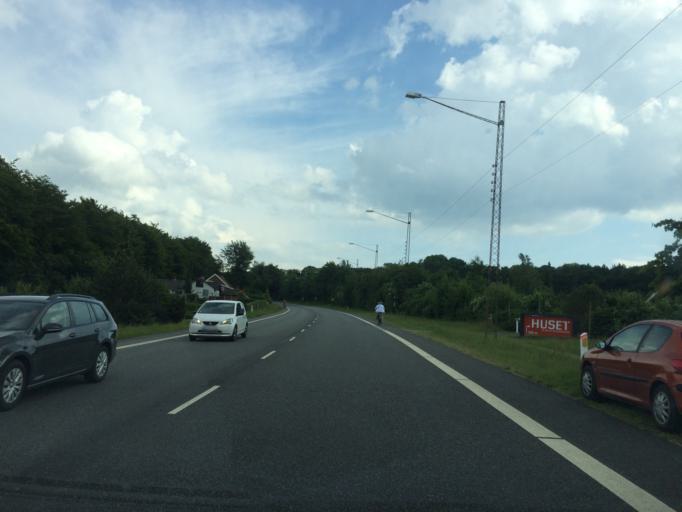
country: DK
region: South Denmark
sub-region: Fredericia Kommune
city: Snoghoj
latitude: 55.5051
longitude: 9.7042
